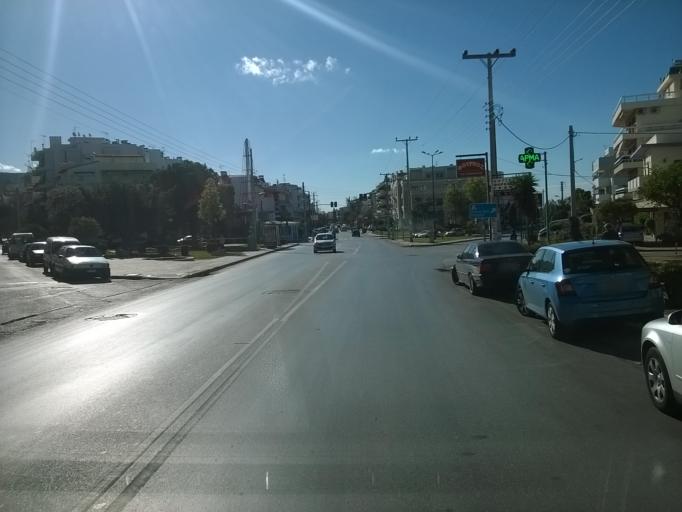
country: GR
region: Attica
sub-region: Nomarchia Athinas
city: Argyroupoli
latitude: 37.8897
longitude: 23.7611
